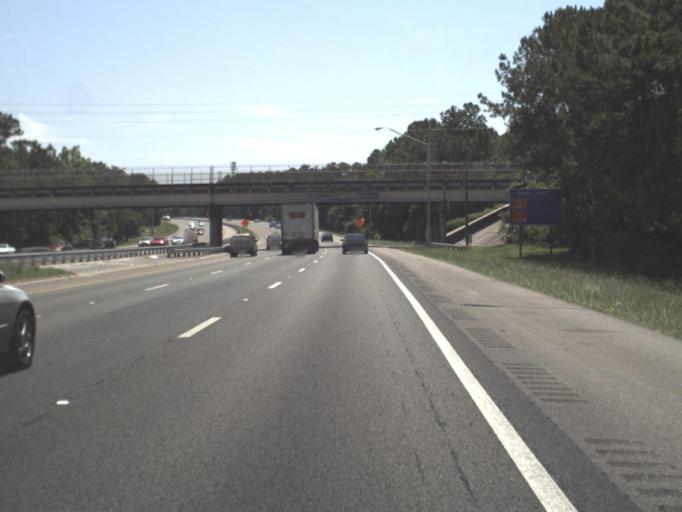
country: US
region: Florida
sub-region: Clay County
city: Bellair-Meadowbrook Terrace
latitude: 30.2855
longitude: -81.7719
